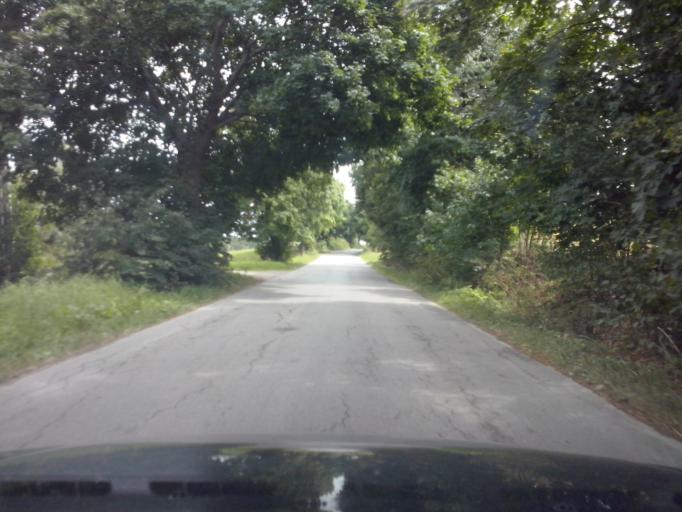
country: PL
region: Swietokrzyskie
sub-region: Powiat kielecki
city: Lagow
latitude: 50.7219
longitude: 21.1115
